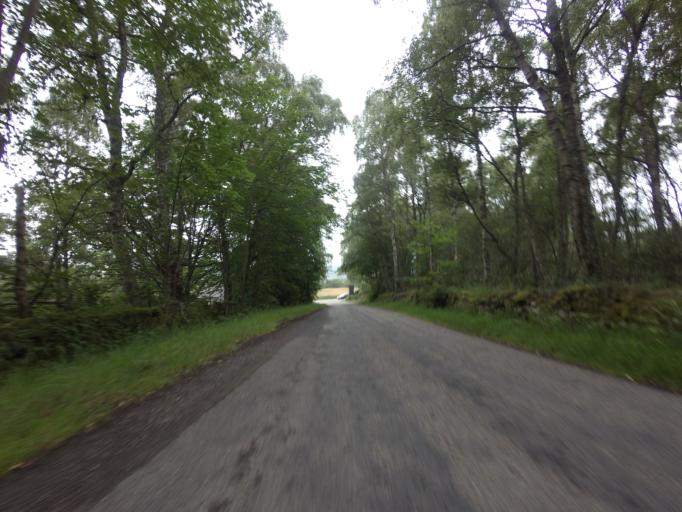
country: GB
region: Scotland
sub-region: Highland
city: Evanton
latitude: 57.8879
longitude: -4.3882
